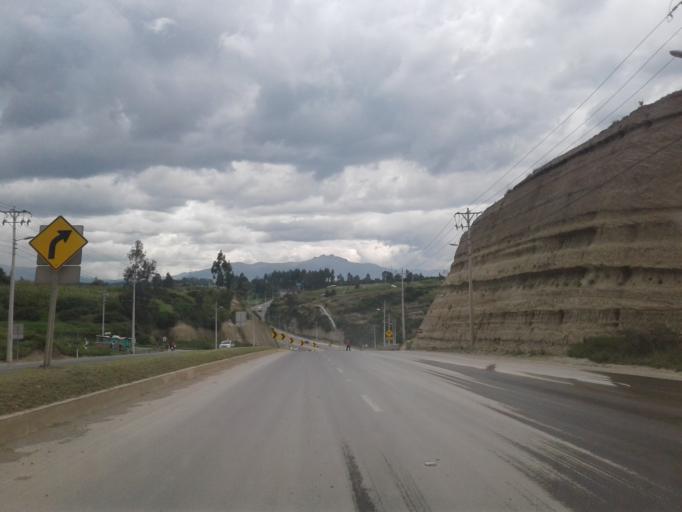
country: EC
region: Pichincha
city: Sangolqui
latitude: -0.3011
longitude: -78.3599
